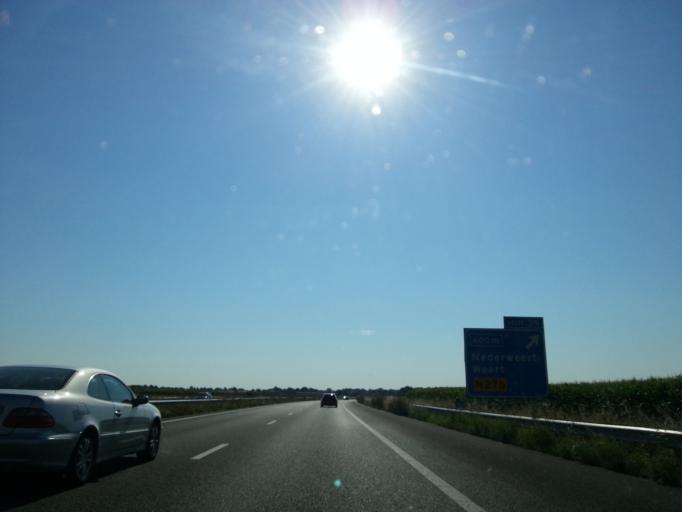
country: NL
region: Limburg
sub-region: Gemeente Nederweert
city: Nederweert
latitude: 51.2827
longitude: 5.7210
